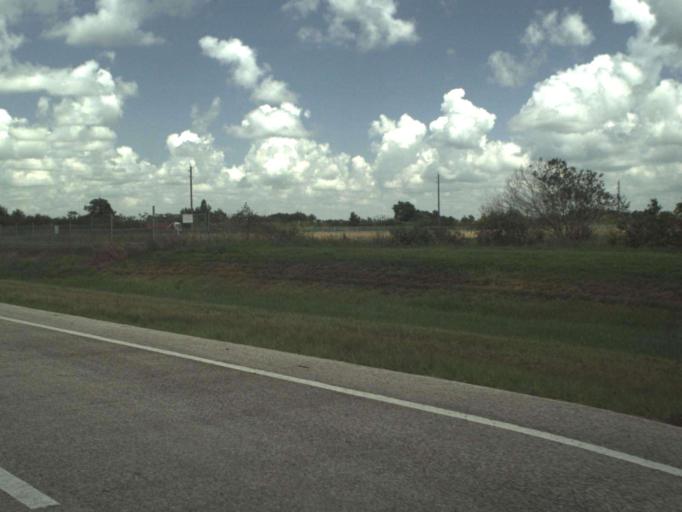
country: US
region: Florida
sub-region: Indian River County
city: Fellsmere
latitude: 27.6405
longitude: -80.6415
